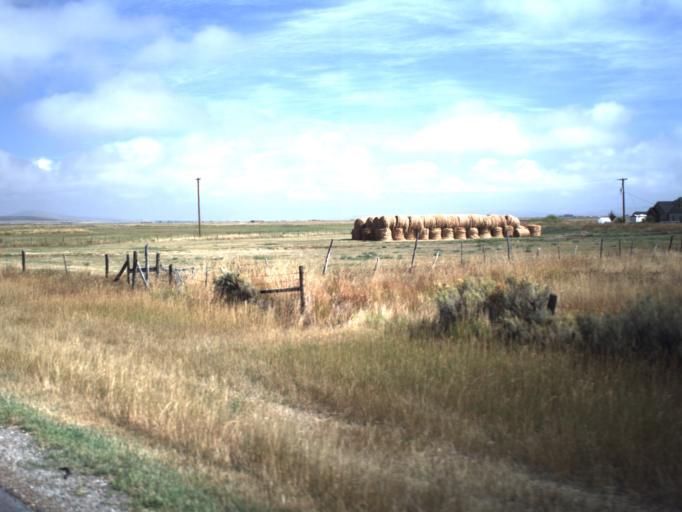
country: US
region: Utah
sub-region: Rich County
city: Randolph
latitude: 41.7138
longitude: -111.1594
